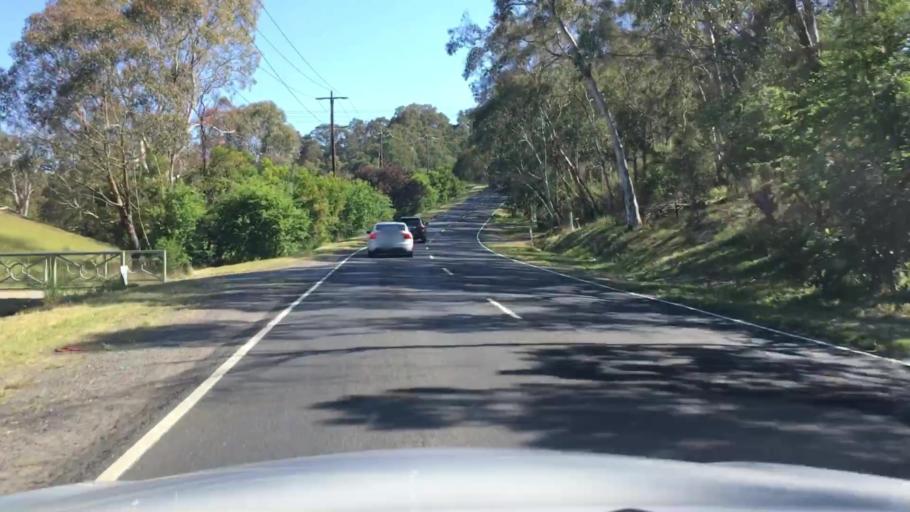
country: AU
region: Victoria
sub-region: Manningham
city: Park Orchards
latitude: -37.7586
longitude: 145.2056
